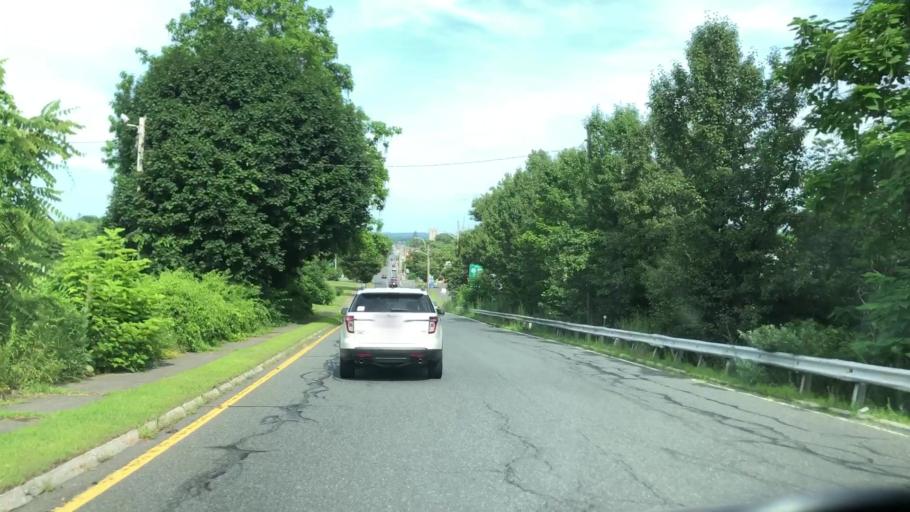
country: US
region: Massachusetts
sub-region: Hampden County
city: Holyoke
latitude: 42.2106
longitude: -72.6325
